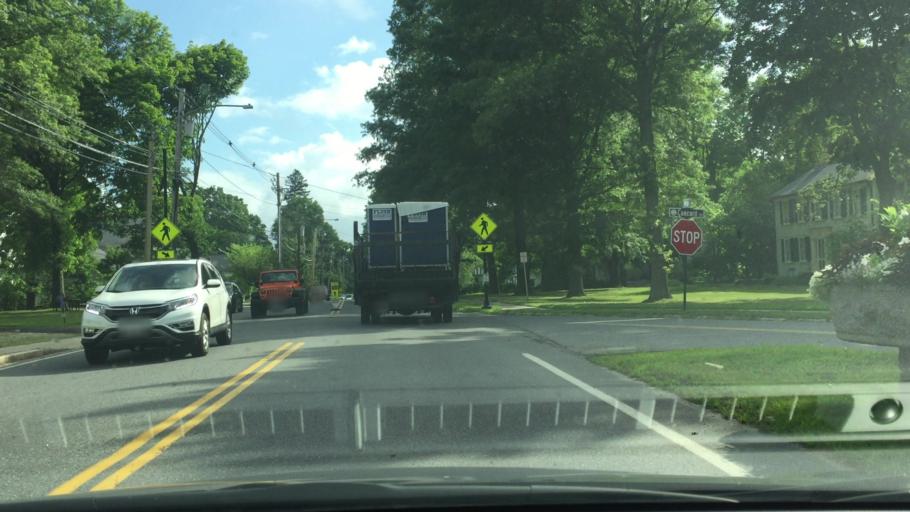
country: US
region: Massachusetts
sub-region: Middlesex County
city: Acton
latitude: 42.4858
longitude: -71.4333
